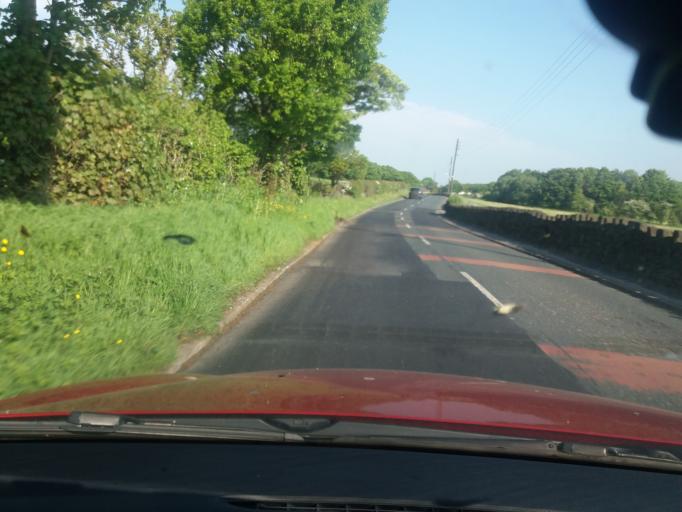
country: GB
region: England
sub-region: Lancashire
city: Adlington
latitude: 53.6317
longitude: -2.5933
